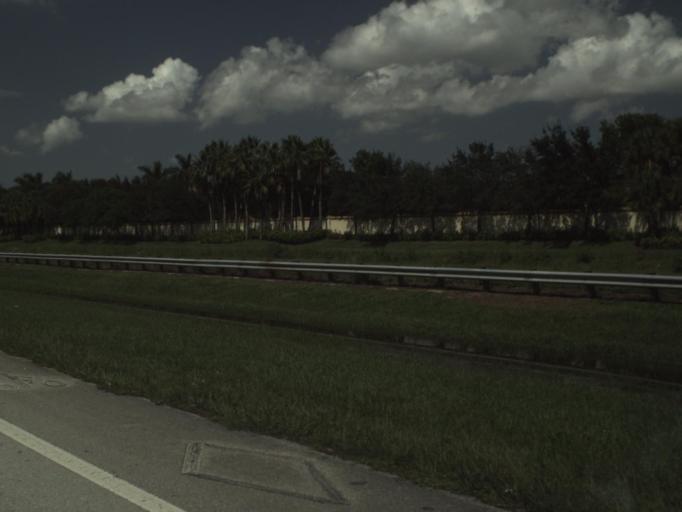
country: US
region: Florida
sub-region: Palm Beach County
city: Wellington
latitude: 26.5805
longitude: -80.2058
